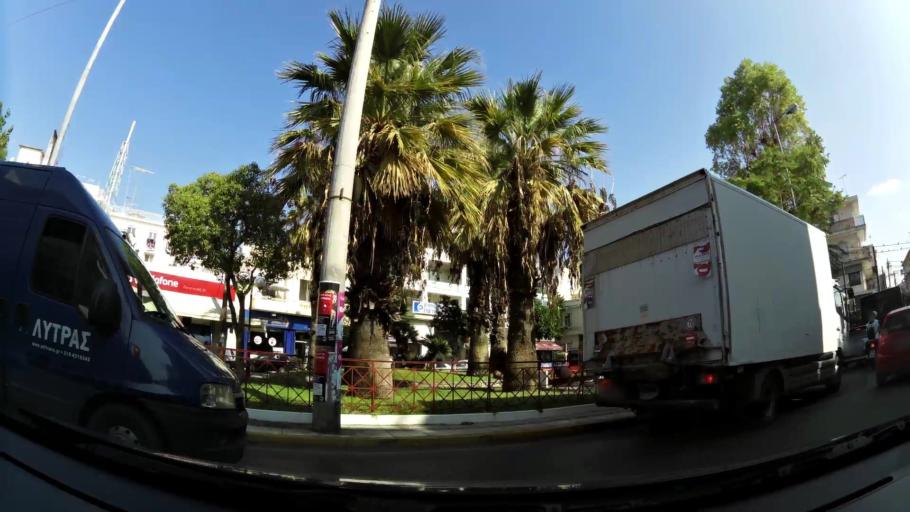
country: GR
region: Attica
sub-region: Nomos Piraios
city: Keratsini
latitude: 37.9579
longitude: 23.6259
